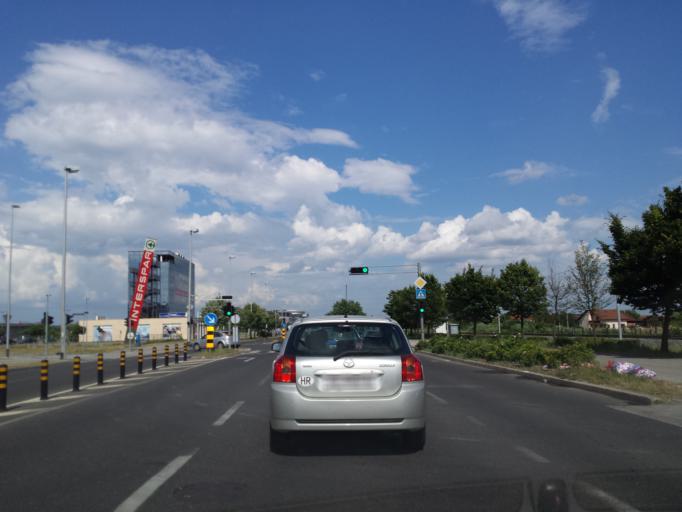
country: HR
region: Grad Zagreb
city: Dubrava
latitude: 45.8234
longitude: 16.0772
